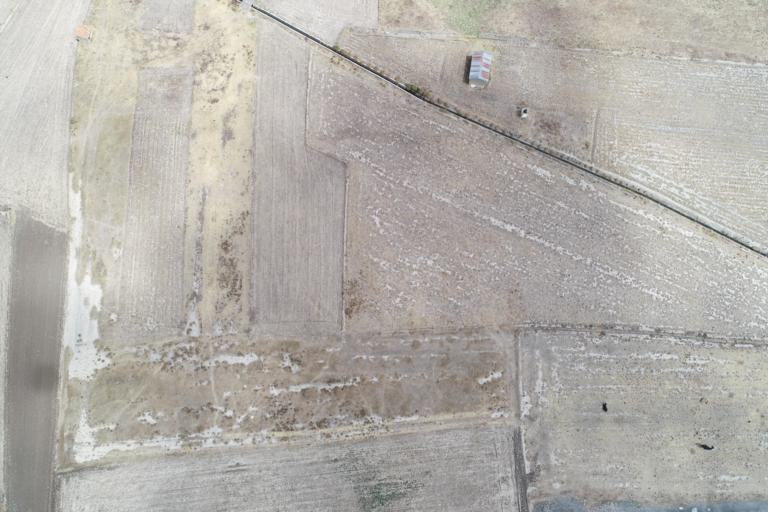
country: BO
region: La Paz
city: Achacachi
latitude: -16.0300
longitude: -68.6899
